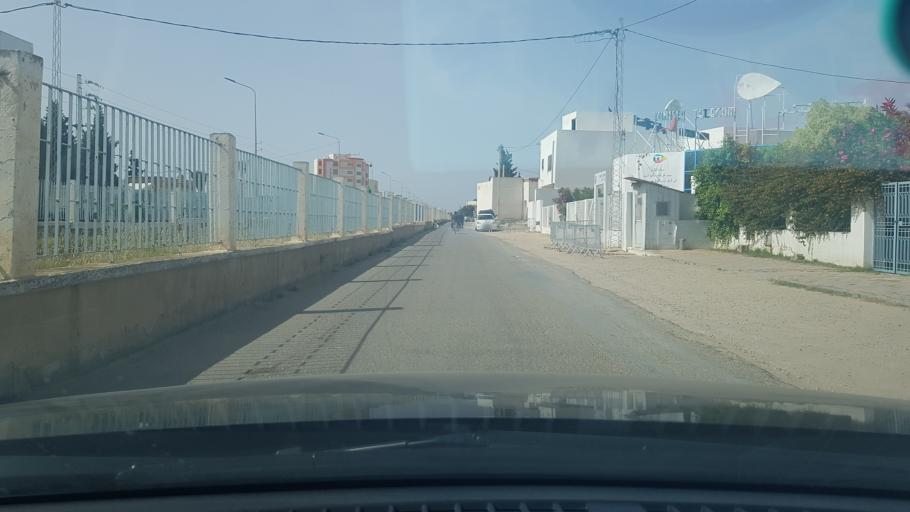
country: TN
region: Safaqis
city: Al Qarmadah
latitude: 34.8056
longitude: 10.7617
